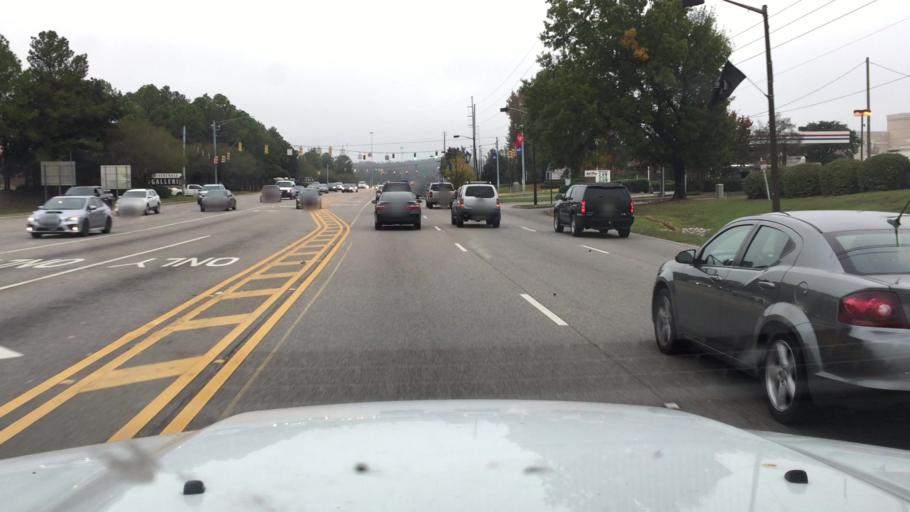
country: US
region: Alabama
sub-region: Jefferson County
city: Hoover
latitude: 33.3774
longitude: -86.8036
